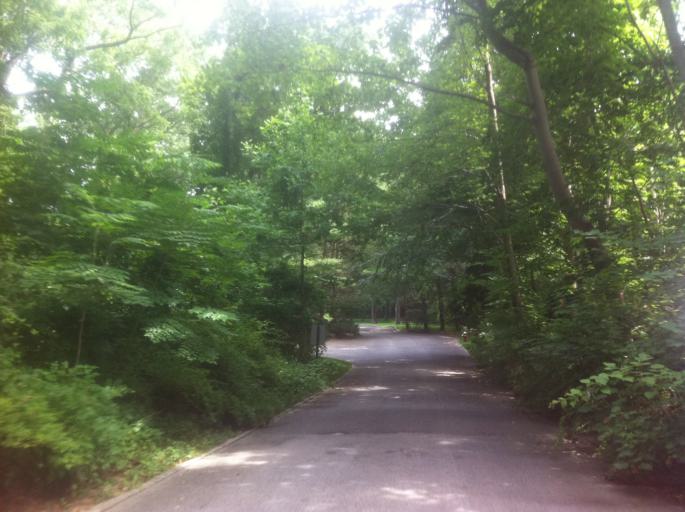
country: US
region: New York
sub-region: Nassau County
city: Locust Valley
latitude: 40.8610
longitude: -73.5784
